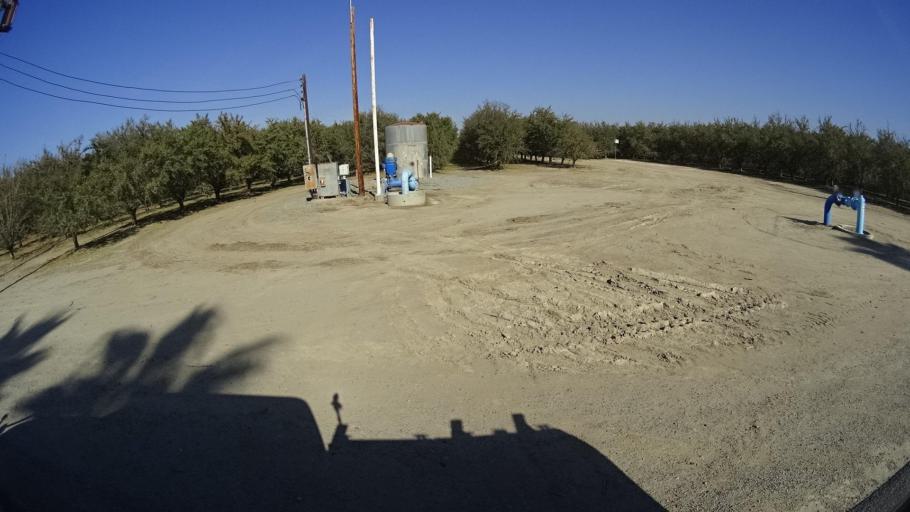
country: US
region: California
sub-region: Kern County
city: Delano
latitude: 35.7177
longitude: -119.3572
